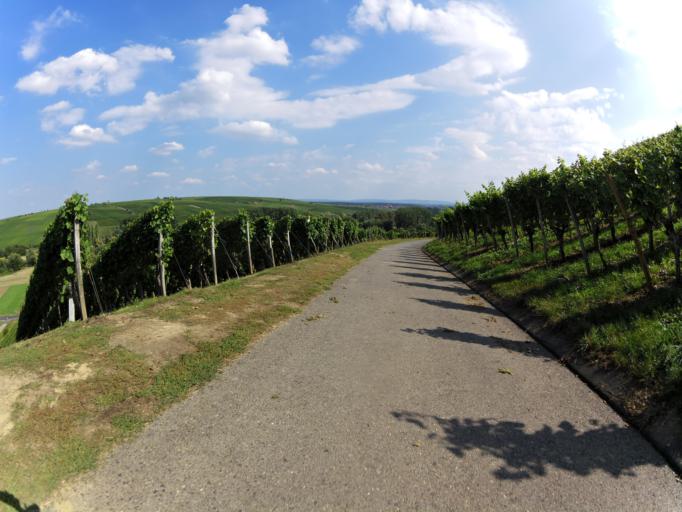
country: DE
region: Bavaria
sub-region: Regierungsbezirk Unterfranken
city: Nordheim
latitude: 49.8390
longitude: 10.1715
